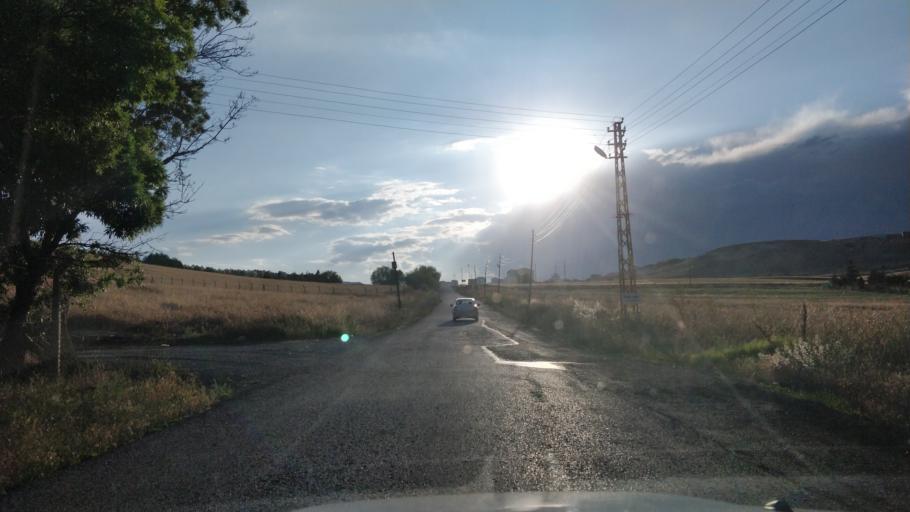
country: TR
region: Ankara
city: Etimesgut
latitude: 39.8264
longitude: 32.5661
